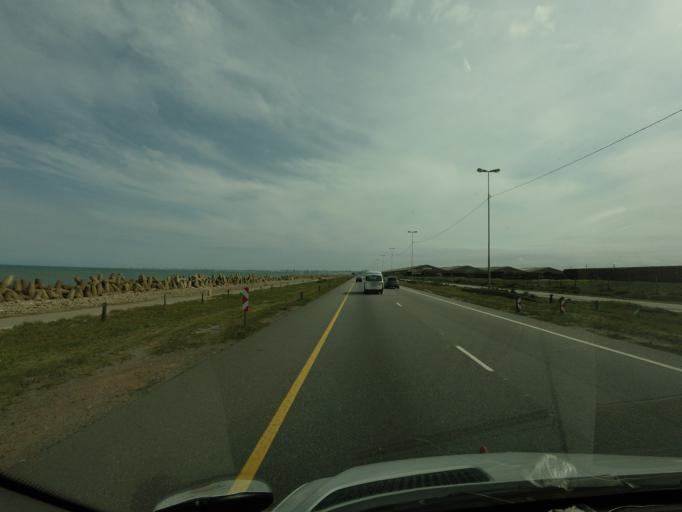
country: ZA
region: Eastern Cape
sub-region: Nelson Mandela Bay Metropolitan Municipality
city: Port Elizabeth
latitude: -33.8994
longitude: 25.6199
